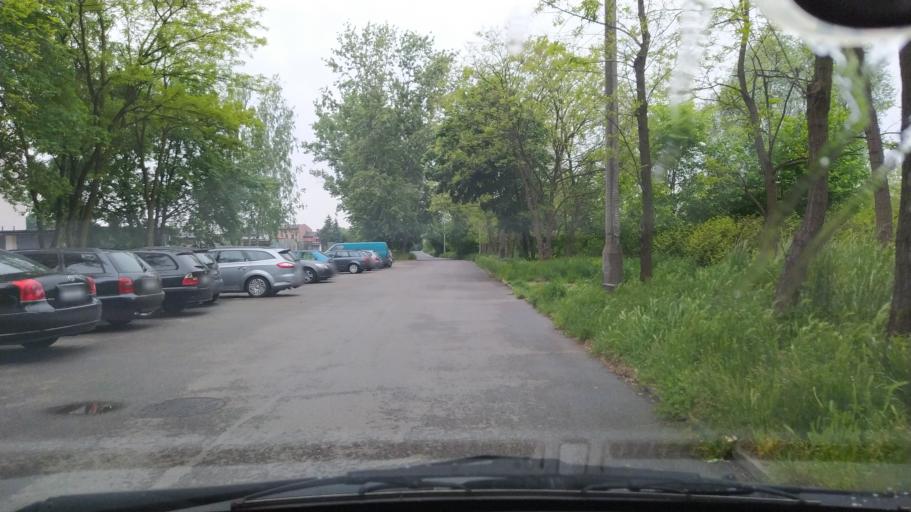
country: PL
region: Silesian Voivodeship
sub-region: Powiat gliwicki
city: Przyszowice
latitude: 50.2956
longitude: 18.7302
